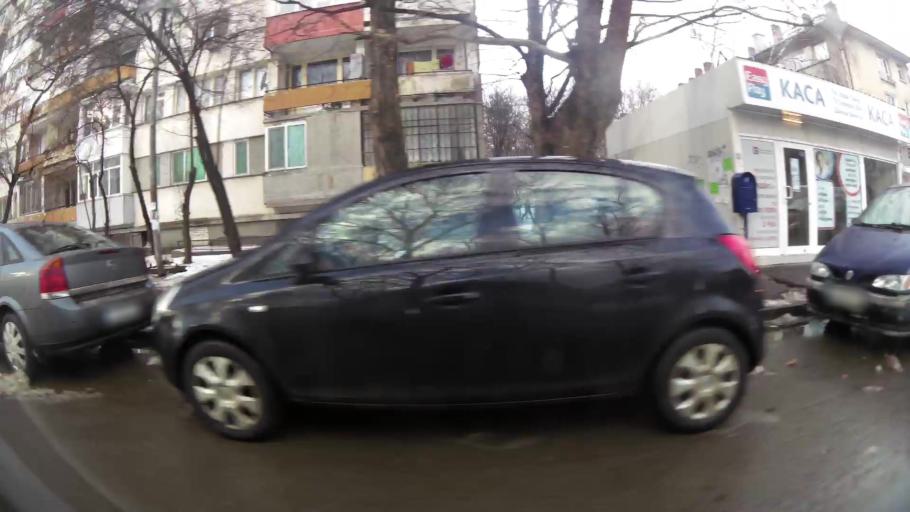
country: BG
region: Sofia-Capital
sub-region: Stolichna Obshtina
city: Sofia
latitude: 42.7028
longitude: 23.2833
